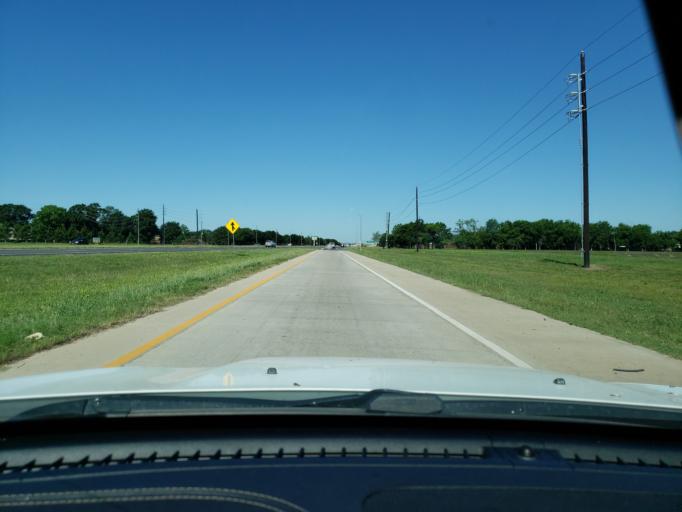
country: US
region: Texas
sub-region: Fort Bend County
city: Pecan Grove
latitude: 29.6605
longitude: -95.7234
